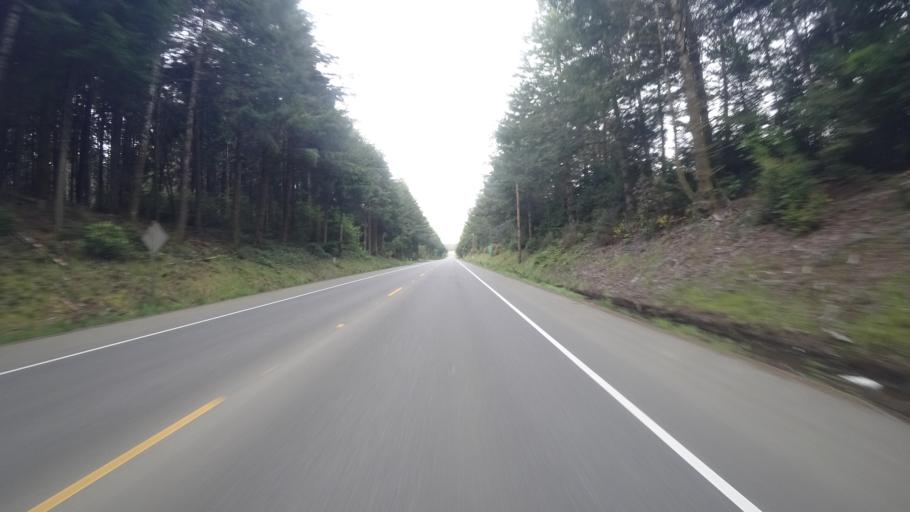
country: US
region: Oregon
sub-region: Coos County
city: Bandon
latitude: 43.1674
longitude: -124.3804
